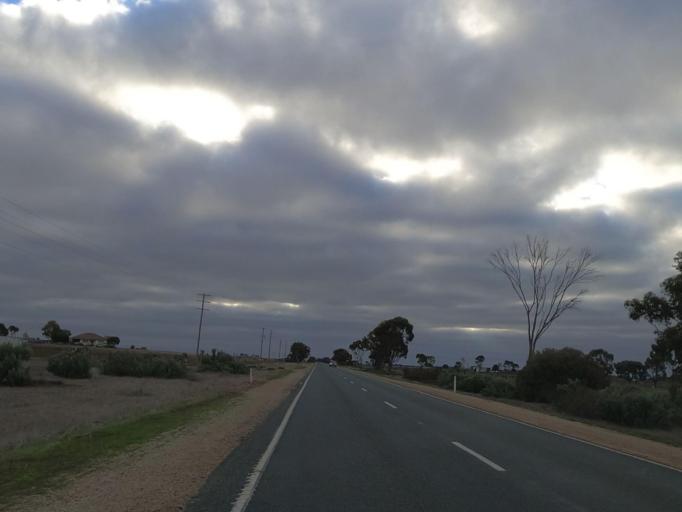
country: AU
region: Victoria
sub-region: Swan Hill
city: Swan Hill
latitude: -35.6427
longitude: 143.8310
